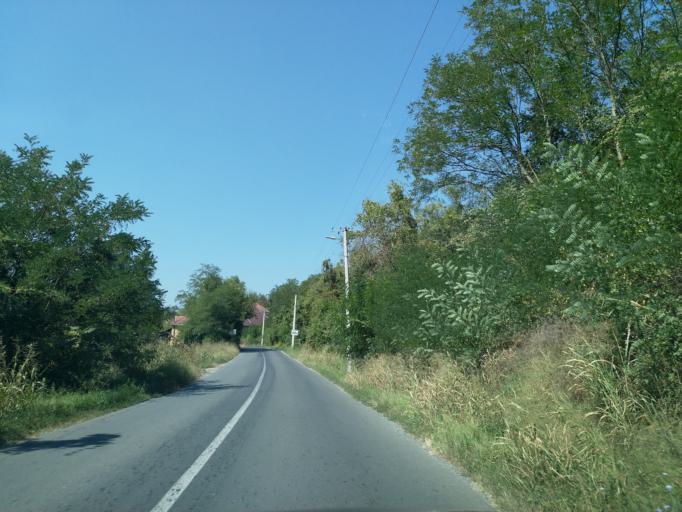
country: RS
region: Central Serbia
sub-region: Rasinski Okrug
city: Krusevac
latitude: 43.6122
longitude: 21.2082
